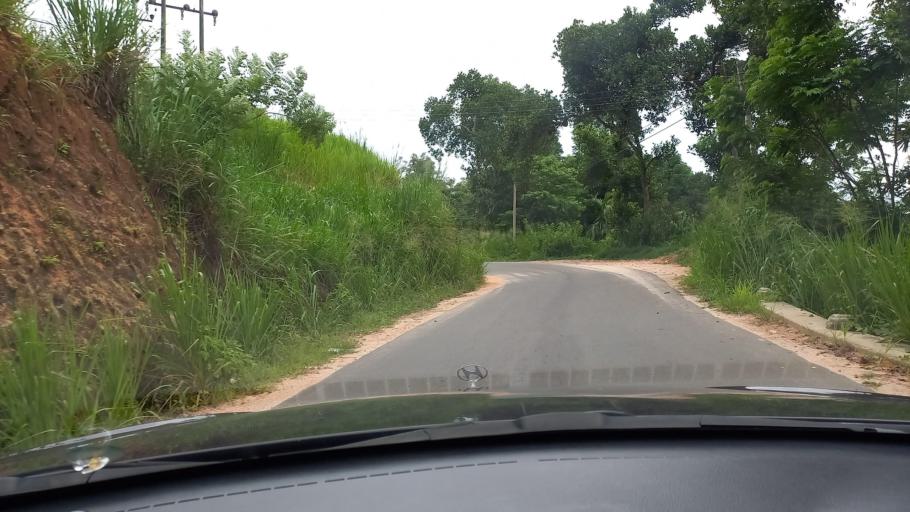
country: LK
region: Central
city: Gampola
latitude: 7.2062
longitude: 80.6256
